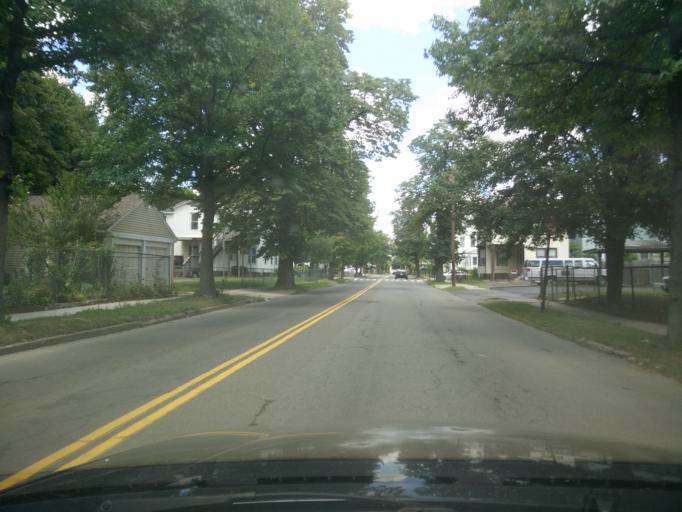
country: US
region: Connecticut
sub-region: New Haven County
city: New Haven
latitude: 41.3337
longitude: -72.9378
